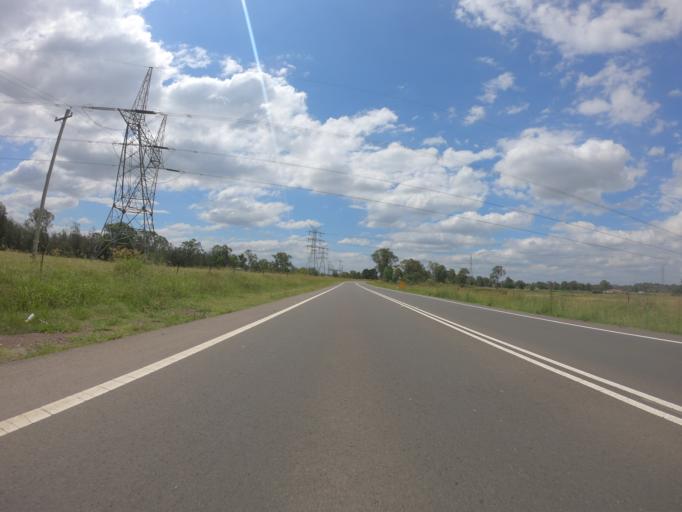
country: AU
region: New South Wales
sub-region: Penrith Municipality
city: Kingswood Park
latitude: -33.8143
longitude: 150.7601
